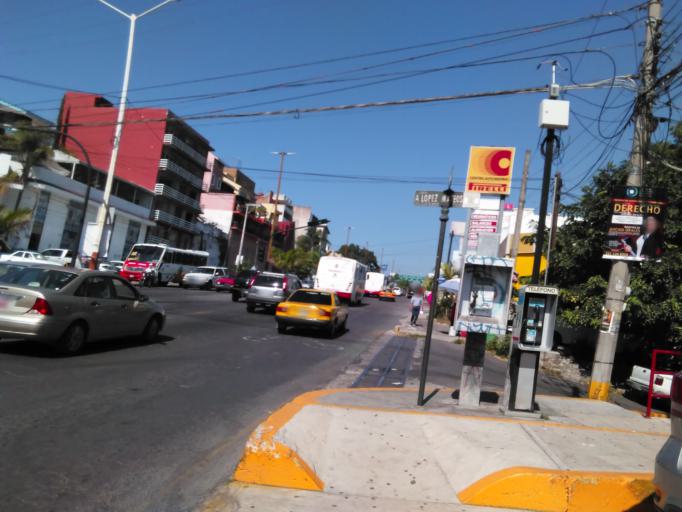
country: MX
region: Nayarit
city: Tepic
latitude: 21.4952
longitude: -104.8966
